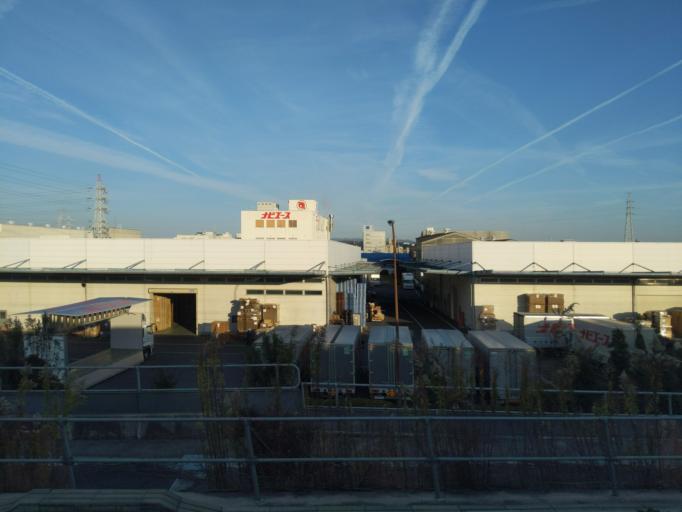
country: JP
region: Aichi
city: Kasugai
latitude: 35.2196
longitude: 136.9525
